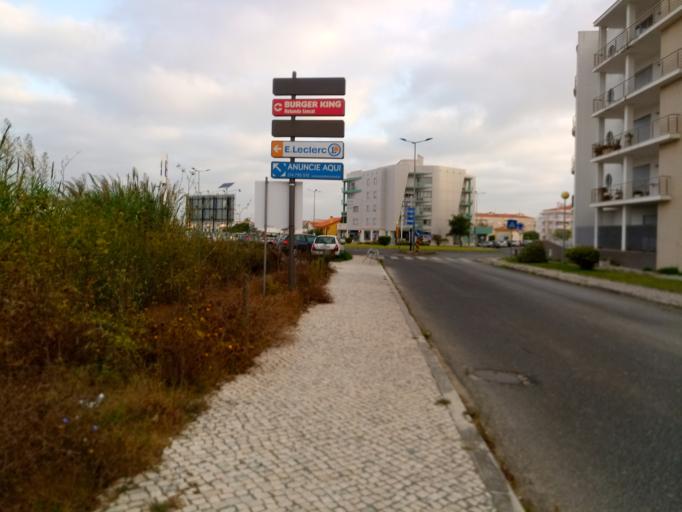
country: PT
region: Leiria
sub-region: Caldas da Rainha
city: Caldas da Rainha
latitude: 39.4122
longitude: -9.1392
